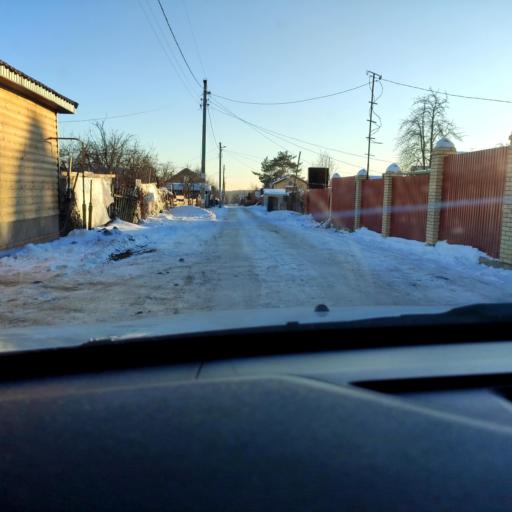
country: RU
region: Samara
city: Petra-Dubrava
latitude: 53.2840
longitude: 50.2918
